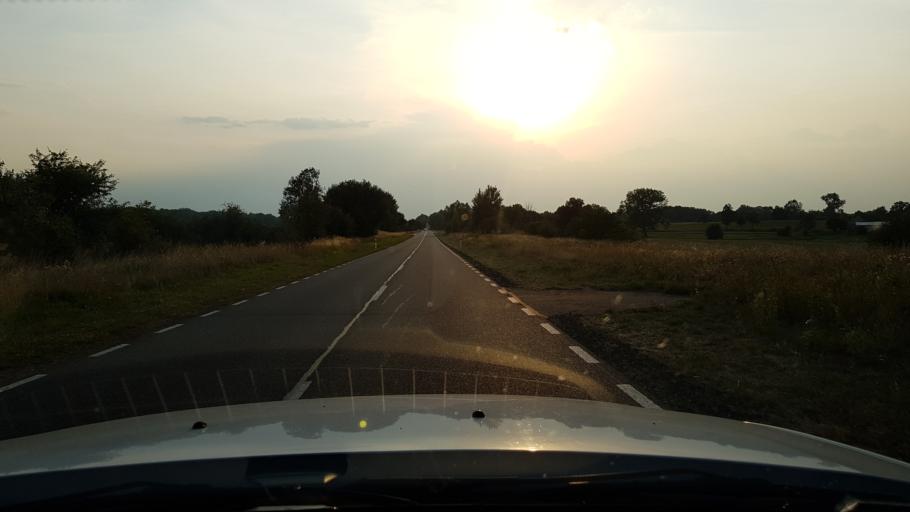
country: PL
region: West Pomeranian Voivodeship
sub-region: Powiat stargardzki
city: Marianowo
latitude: 53.4275
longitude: 15.2532
